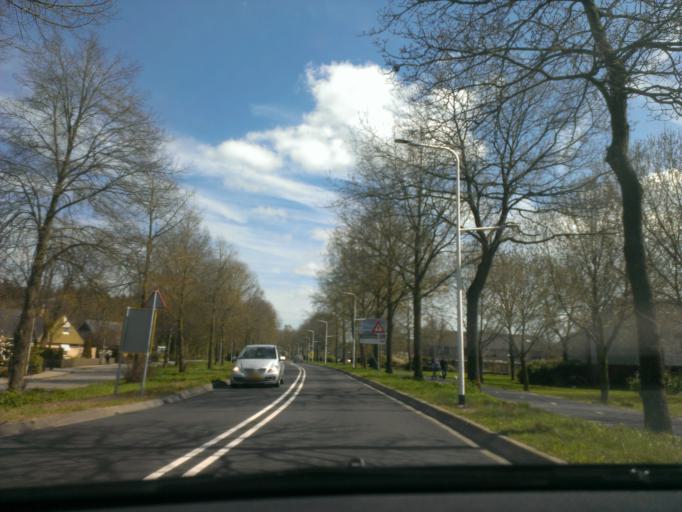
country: NL
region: Overijssel
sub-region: Gemeente Olst-Wijhe
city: Wijhe
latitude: 52.3841
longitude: 6.1373
